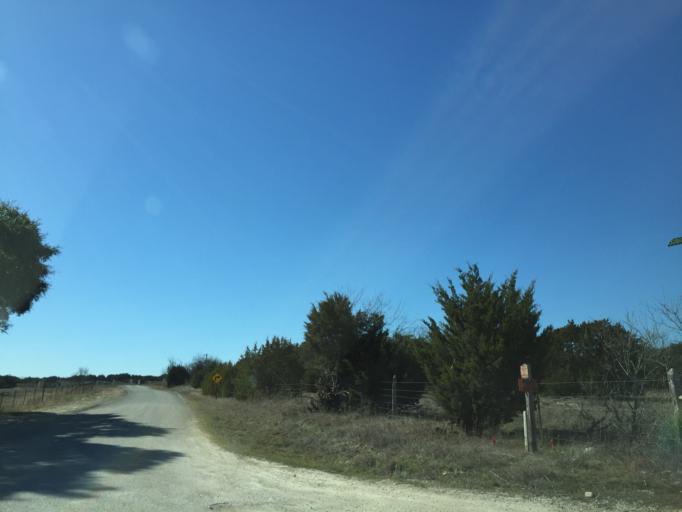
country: US
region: Texas
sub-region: Burnet County
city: Bertram
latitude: 30.9034
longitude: -98.1037
